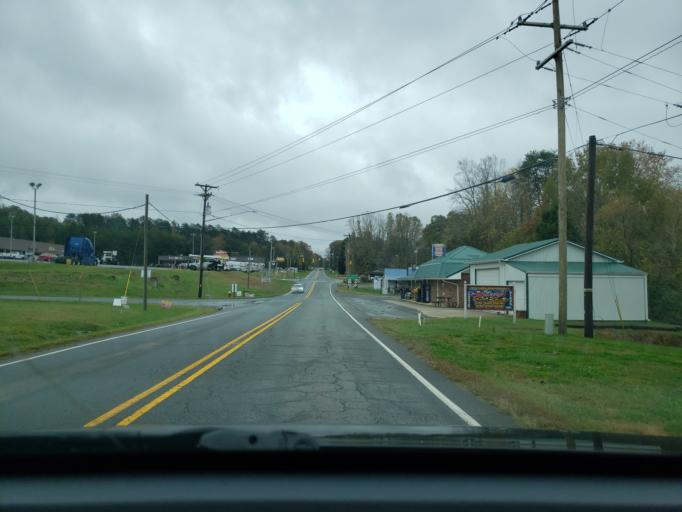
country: US
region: North Carolina
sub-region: Stokes County
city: Walnut Cove
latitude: 36.2822
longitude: -80.1457
